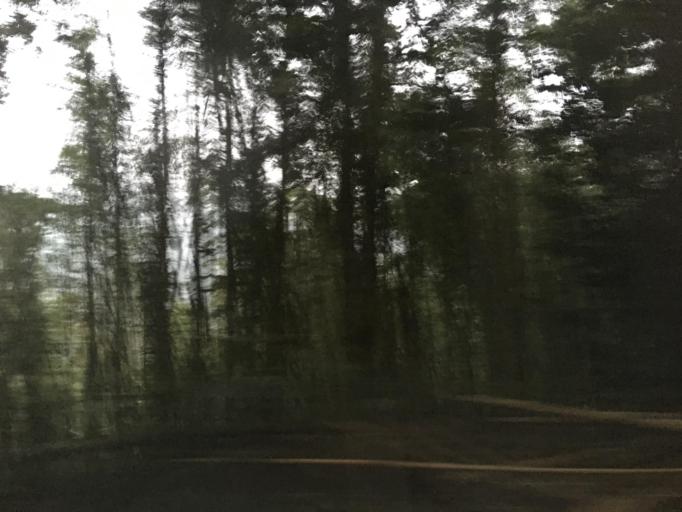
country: TW
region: Taiwan
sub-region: Chiayi
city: Jiayi Shi
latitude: 23.5116
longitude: 120.6587
